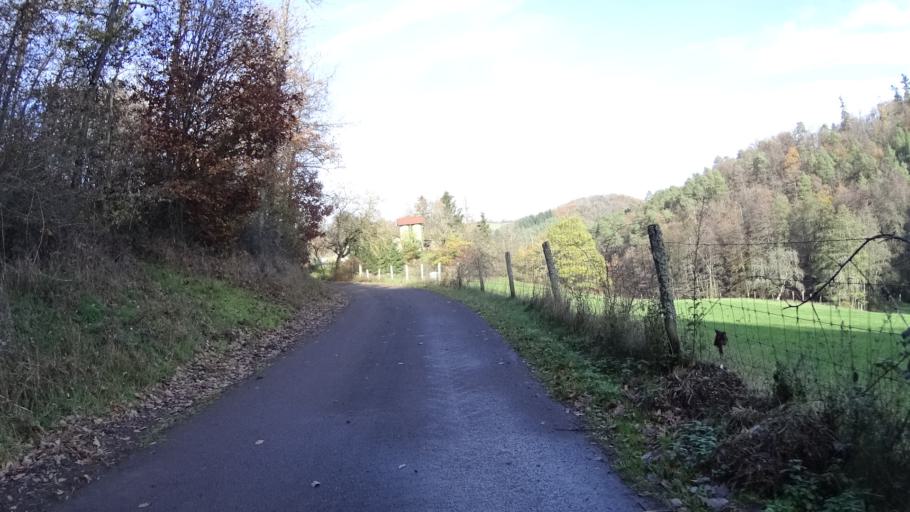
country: DE
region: Rheinland-Pfalz
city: Unterjeckenbach
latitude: 49.6602
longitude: 7.4923
